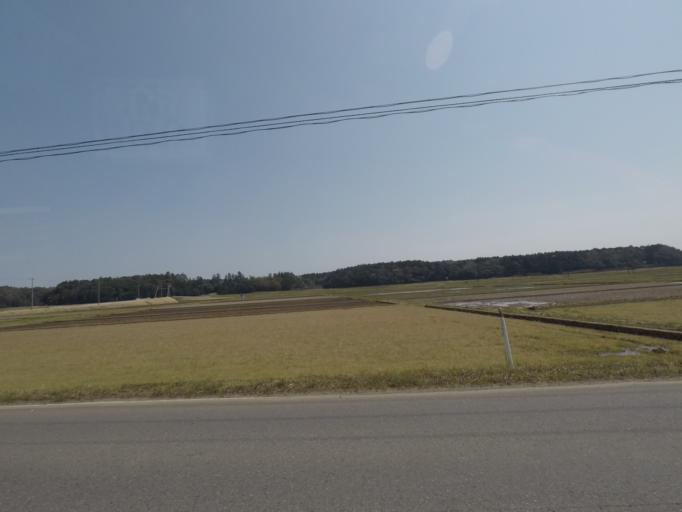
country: JP
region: Chiba
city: Yokaichiba
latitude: 35.7659
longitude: 140.4836
